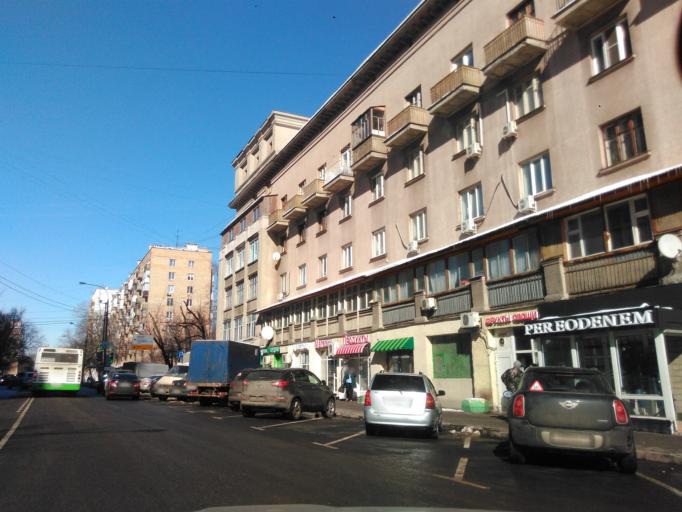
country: RU
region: Moskovskaya
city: Dorogomilovo
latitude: 55.7975
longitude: 37.5686
